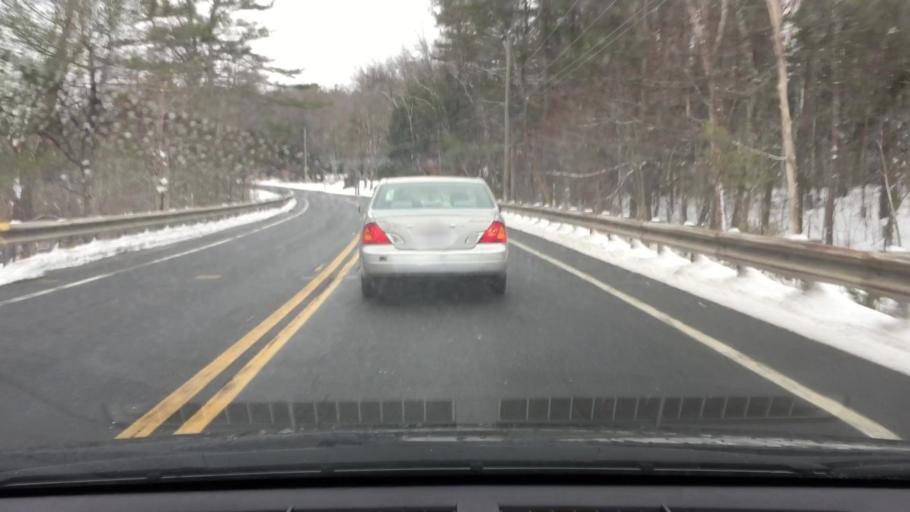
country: US
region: Massachusetts
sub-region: Hampshire County
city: Pelham
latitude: 42.3483
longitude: -72.4044
